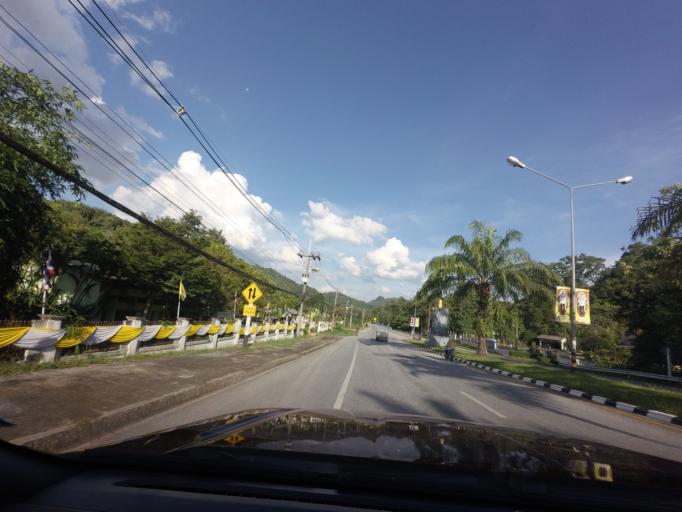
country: TH
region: Yala
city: Than To
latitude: 6.1645
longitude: 101.1824
